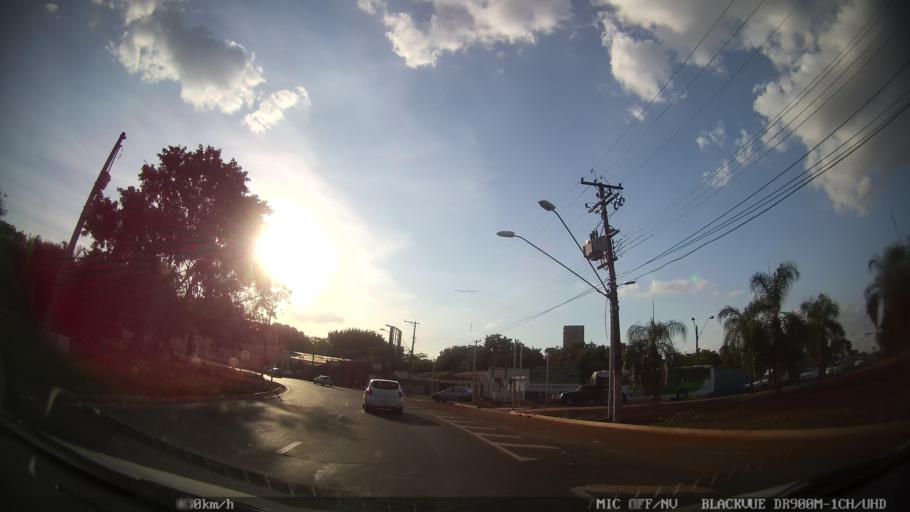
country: BR
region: Sao Paulo
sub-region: Ribeirao Preto
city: Ribeirao Preto
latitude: -21.1662
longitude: -47.8137
